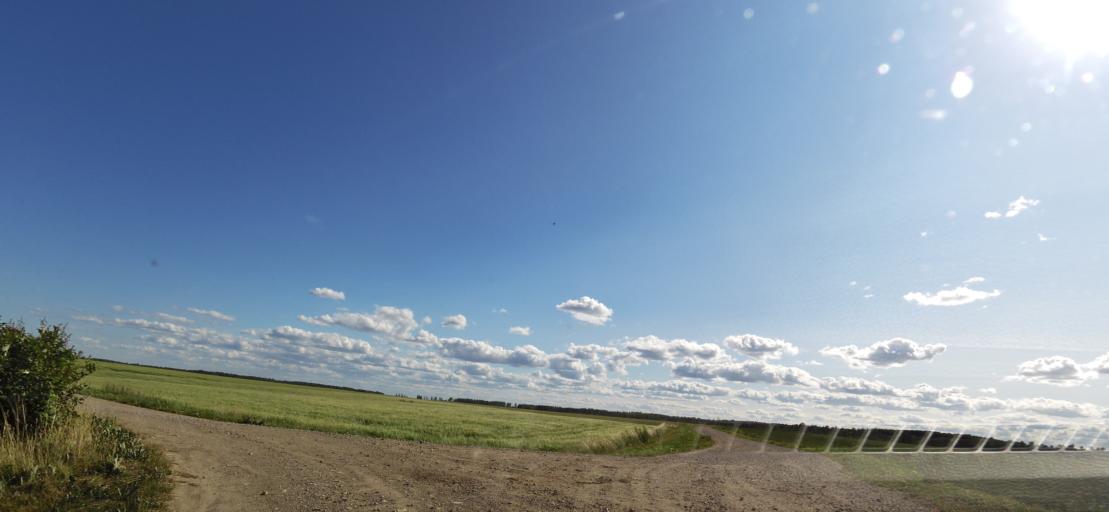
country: LT
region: Panevezys
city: Pasvalys
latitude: 56.1689
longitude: 24.4264
